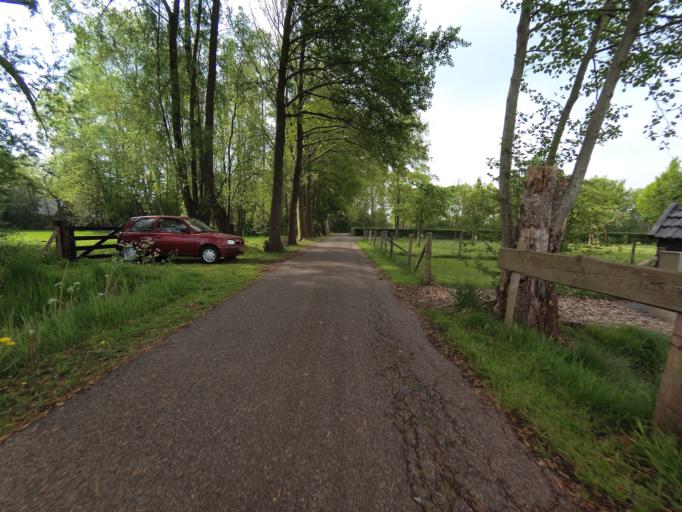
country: NL
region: Gelderland
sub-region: Gemeente Barneveld
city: Terschuur
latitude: 52.1369
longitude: 5.5207
